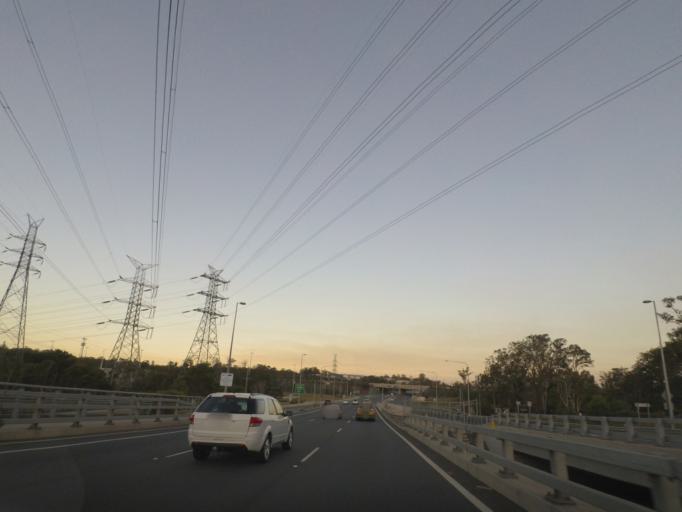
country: AU
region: Queensland
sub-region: Brisbane
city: Mackenzie
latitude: -27.5459
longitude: 153.1136
